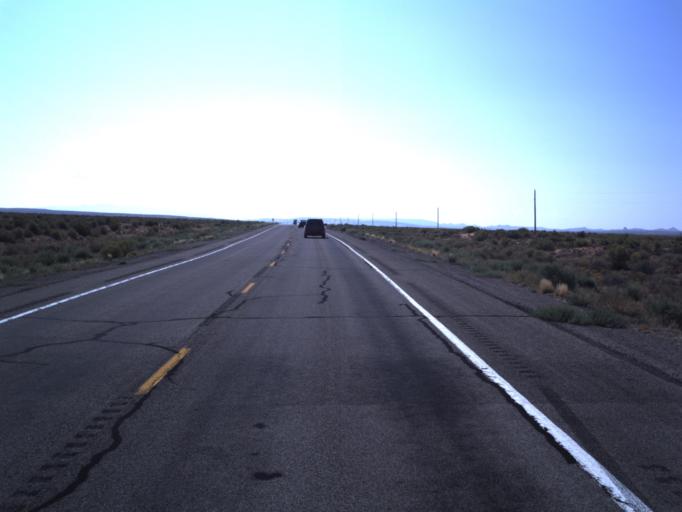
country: US
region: Utah
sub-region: San Juan County
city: Blanding
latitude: 37.2028
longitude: -109.6056
